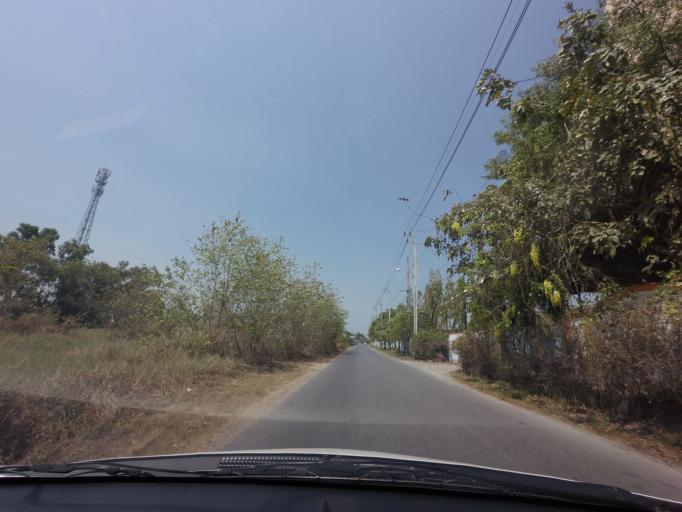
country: TH
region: Bangkok
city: Nong Chok
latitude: 13.8621
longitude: 100.8531
